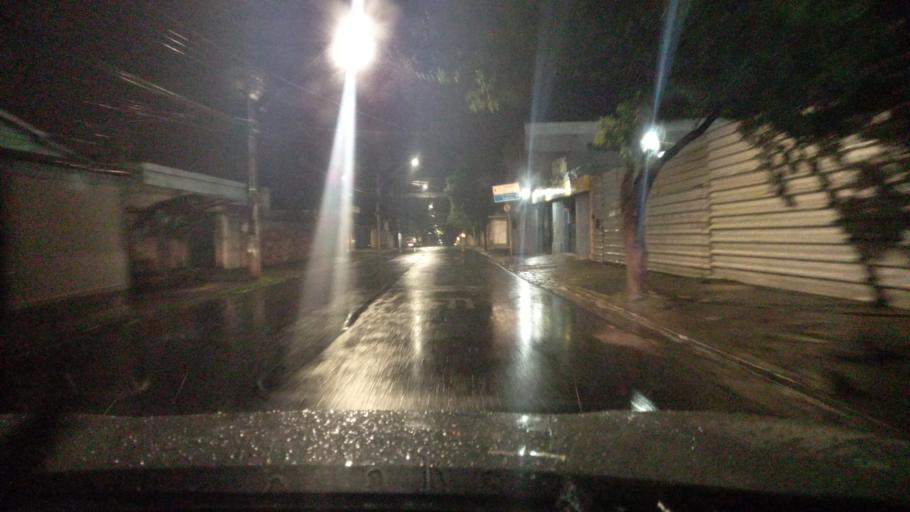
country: BR
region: Minas Gerais
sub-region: Belo Horizonte
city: Belo Horizonte
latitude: -19.9060
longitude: -43.9068
